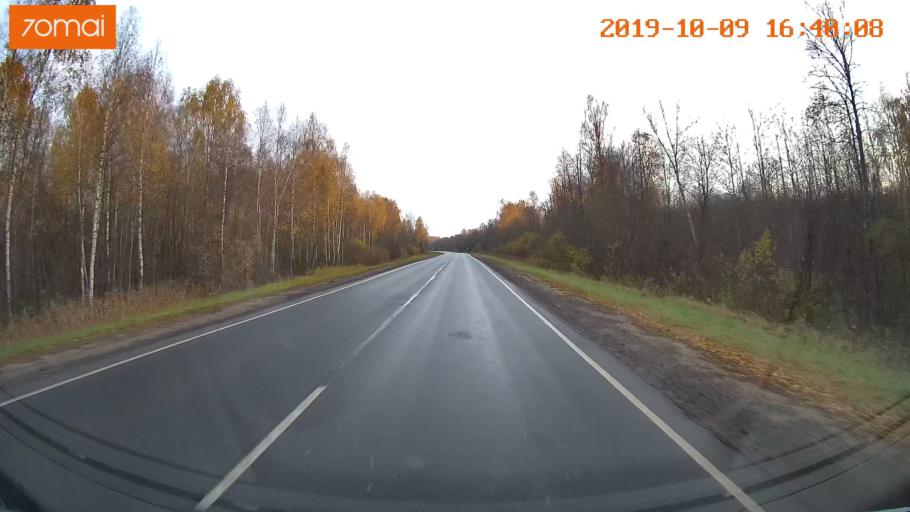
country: RU
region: Kostroma
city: Volgorechensk
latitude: 57.4878
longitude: 41.0569
